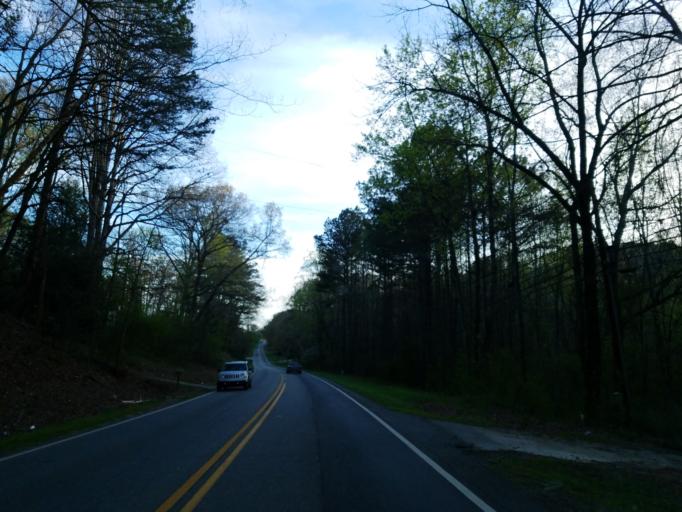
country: US
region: Georgia
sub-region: Cherokee County
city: Canton
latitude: 34.2650
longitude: -84.4610
